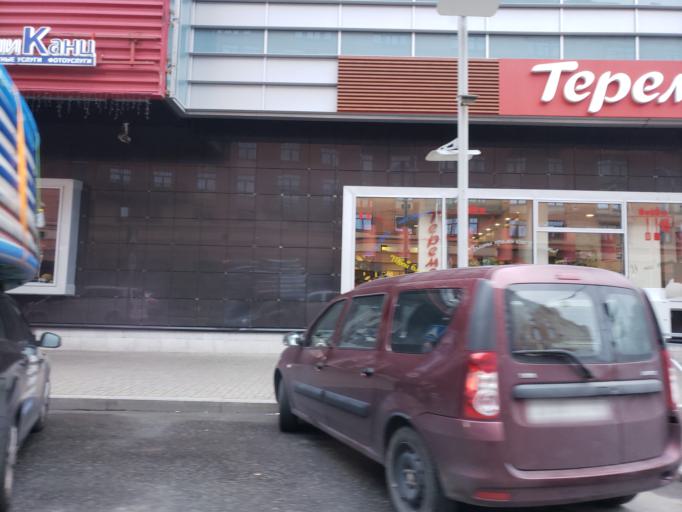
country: RU
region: St.-Petersburg
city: Vasyl'evsky Ostrov
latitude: 59.9391
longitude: 30.2289
